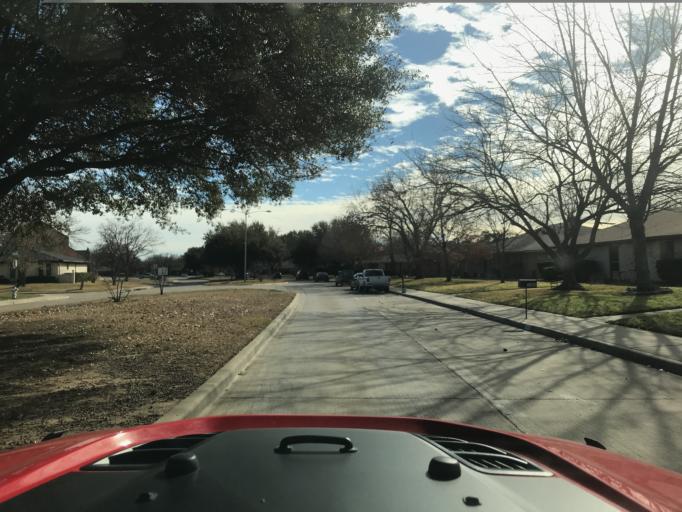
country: US
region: Texas
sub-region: Denton County
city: Lewisville
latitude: 33.0480
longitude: -97.0290
